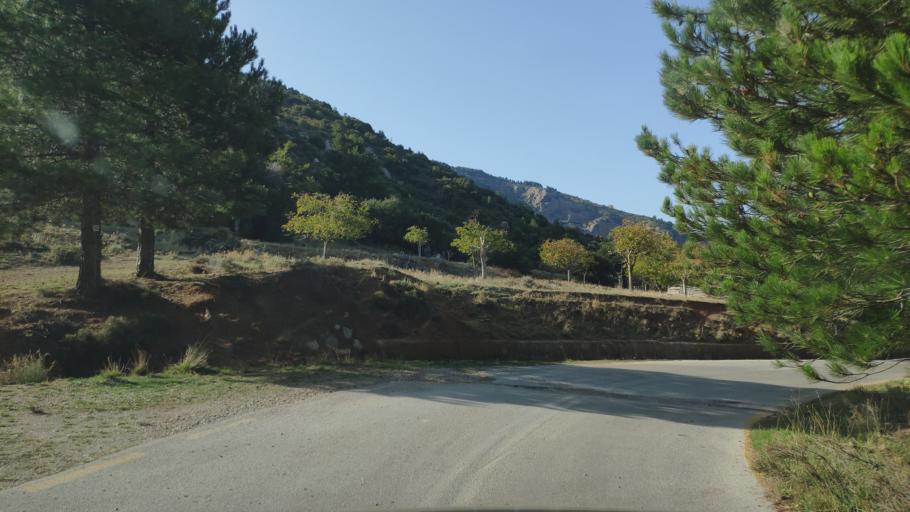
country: GR
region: West Greece
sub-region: Nomos Achaias
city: Aiyira
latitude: 38.0567
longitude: 22.3817
